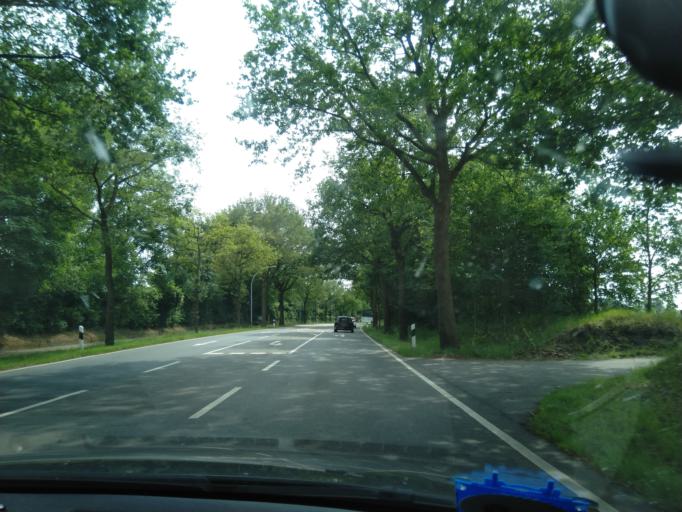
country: DE
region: Lower Saxony
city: Nordhorn
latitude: 52.4457
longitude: 7.0522
